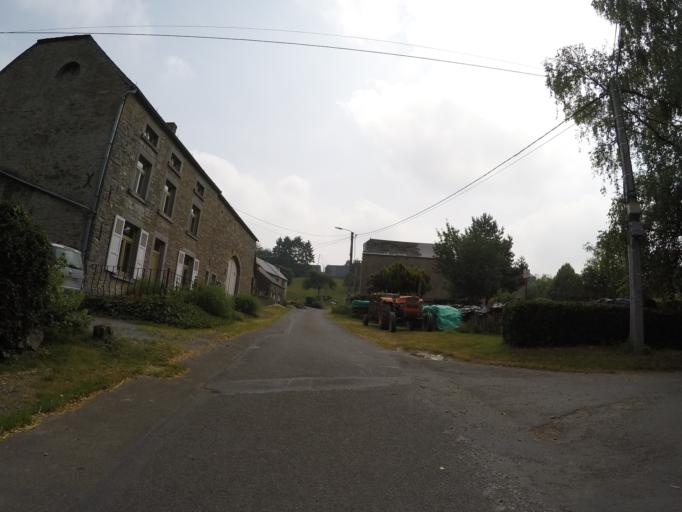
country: BE
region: Wallonia
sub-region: Province de Namur
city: Assesse
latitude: 50.3405
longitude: 4.9711
